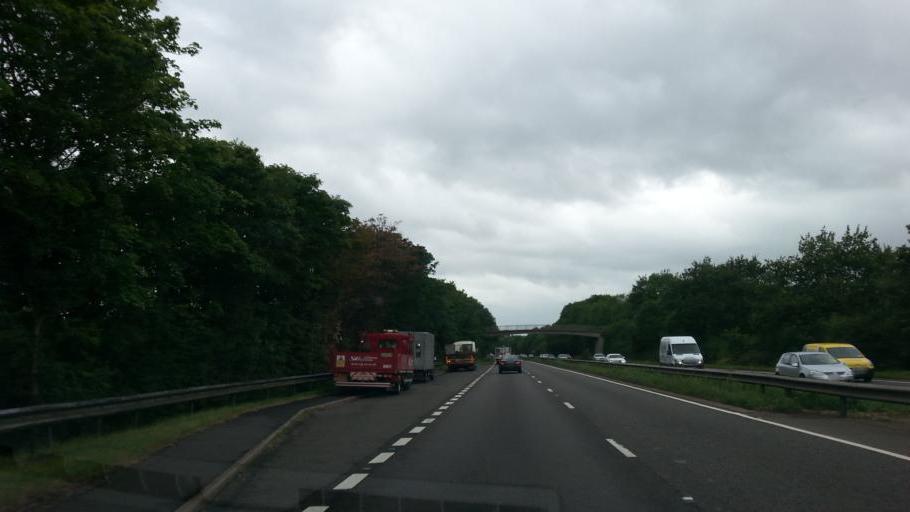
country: GB
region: England
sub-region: Warwickshire
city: Warwick
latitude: 52.2959
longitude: -1.5986
